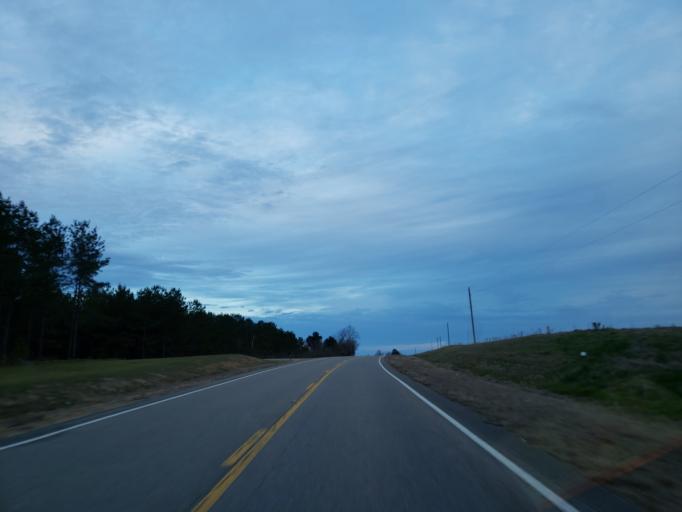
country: US
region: Mississippi
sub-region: Kemper County
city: De Kalb
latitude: 32.8309
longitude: -88.3890
